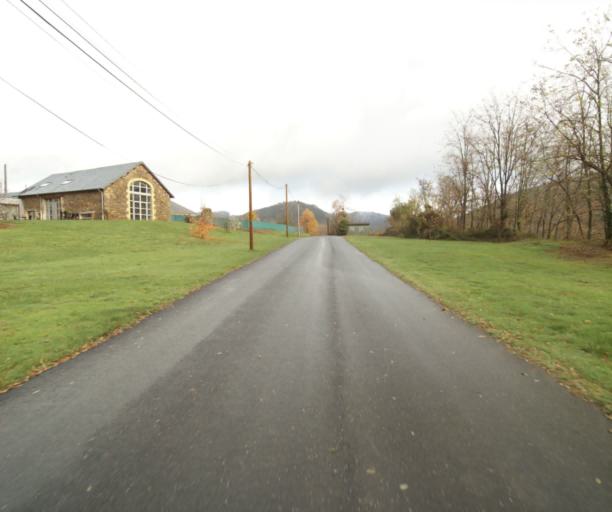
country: FR
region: Limousin
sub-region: Departement de la Correze
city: Cornil
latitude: 45.1980
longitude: 1.6532
